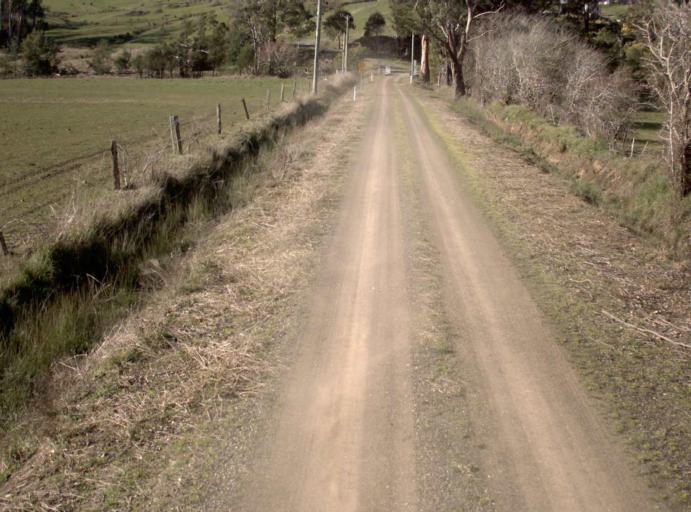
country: AU
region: Tasmania
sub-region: Launceston
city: Mayfield
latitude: -41.2547
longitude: 147.1544
